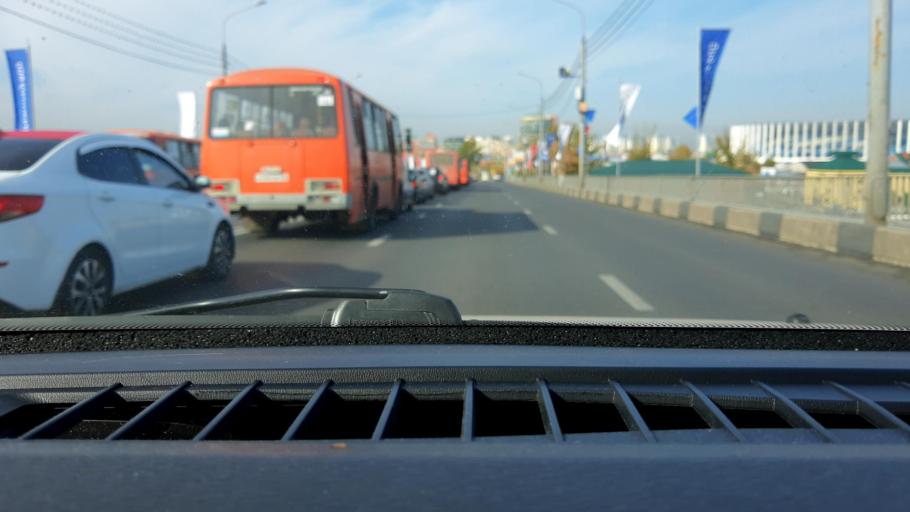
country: RU
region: Nizjnij Novgorod
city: Nizhniy Novgorod
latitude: 56.3284
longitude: 43.9745
